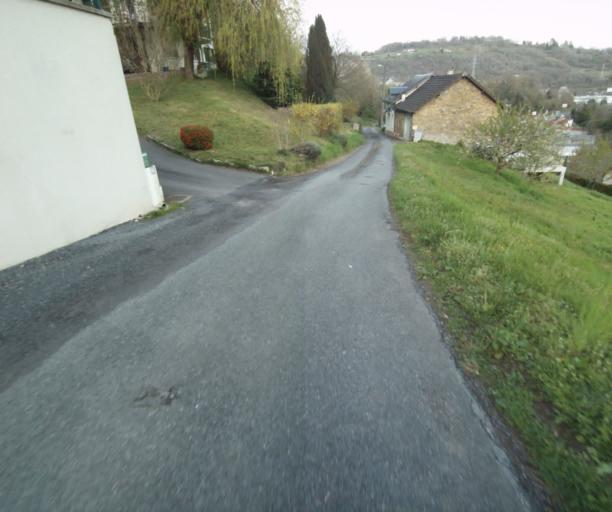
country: FR
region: Limousin
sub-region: Departement de la Correze
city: Tulle
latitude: 45.2525
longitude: 1.7516
